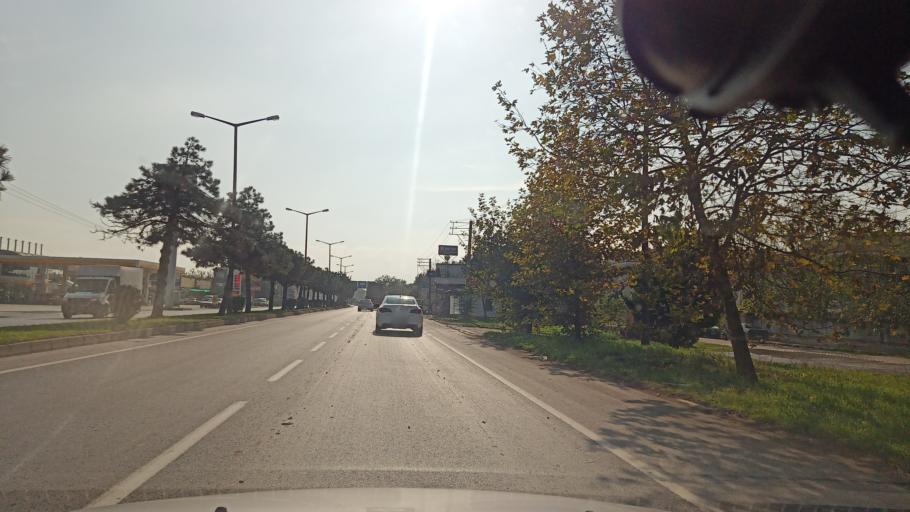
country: TR
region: Sakarya
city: Adapazari
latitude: 40.8050
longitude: 30.4058
